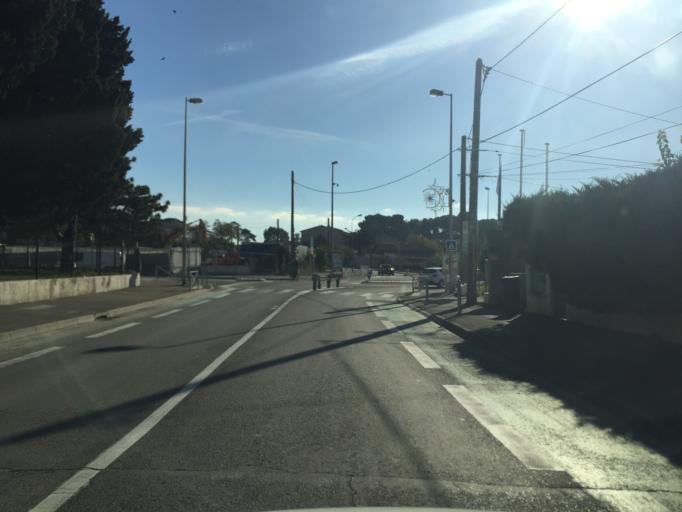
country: FR
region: Provence-Alpes-Cote d'Azur
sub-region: Departement des Bouches-du-Rhone
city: Salon-de-Provence
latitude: 43.6481
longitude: 5.1021
